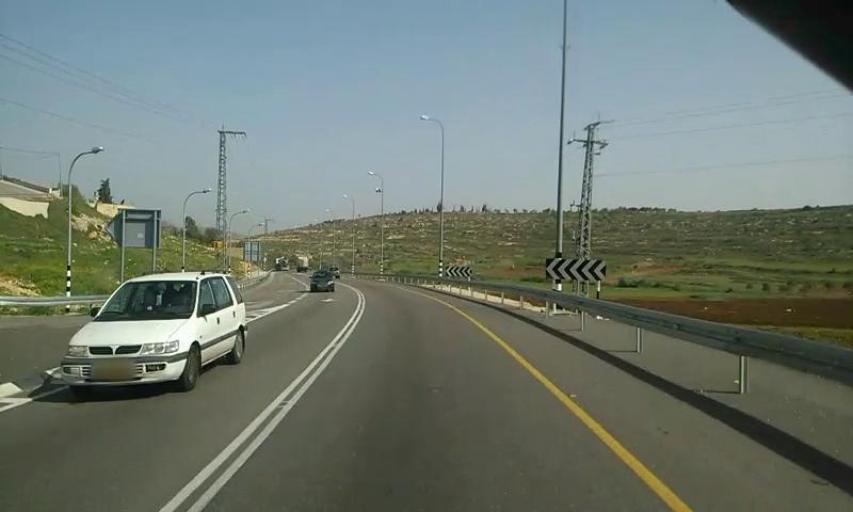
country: PS
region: West Bank
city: Sinjil
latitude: 32.0292
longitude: 35.2723
